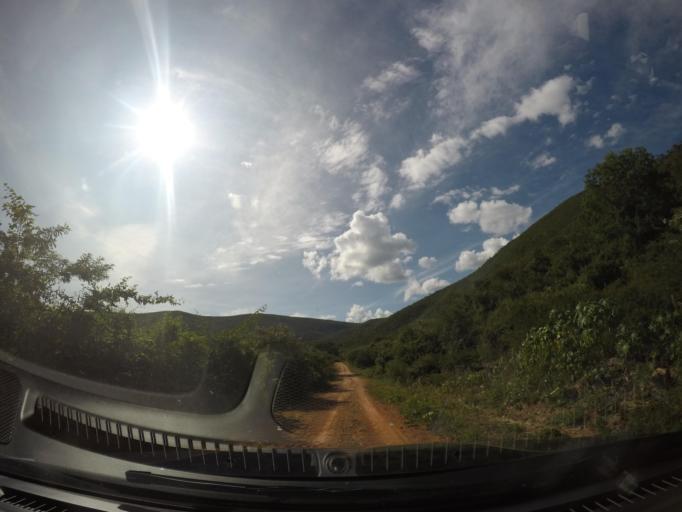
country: BR
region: Bahia
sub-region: Barra Da Estiva
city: Barra da Estiva
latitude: -13.1953
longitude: -41.5929
